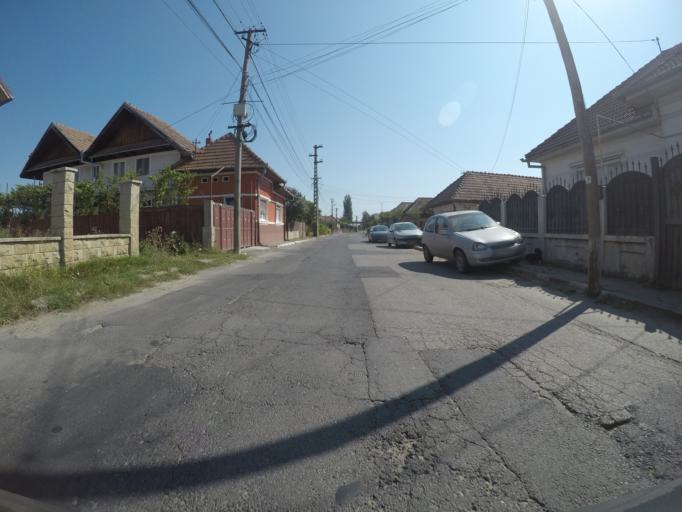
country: RO
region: Brasov
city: Fogarasch
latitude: 45.8281
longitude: 24.9796
